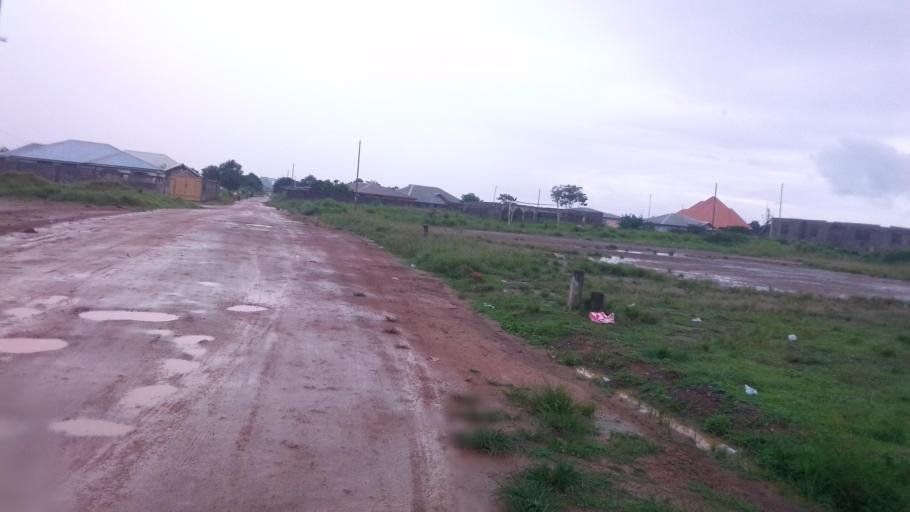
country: SL
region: Eastern Province
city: Hangha
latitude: 7.9132
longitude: -11.1650
